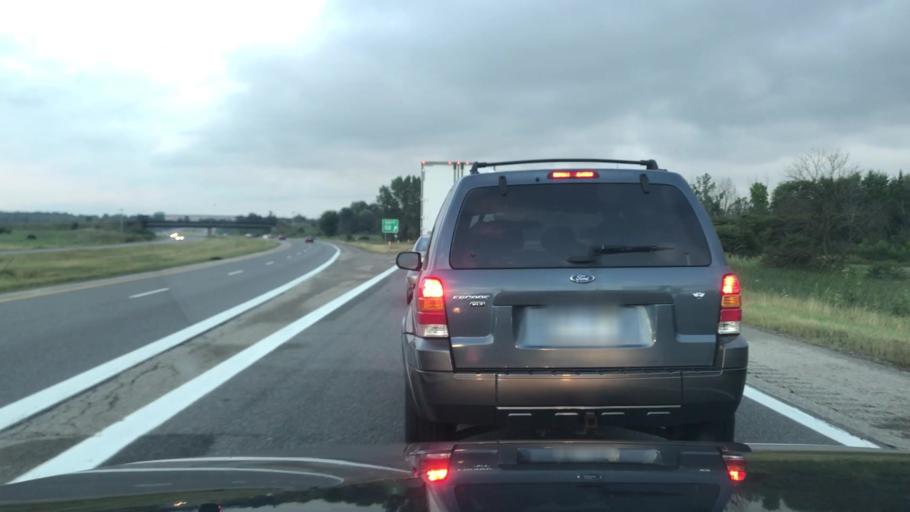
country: US
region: Michigan
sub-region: Ottawa County
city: Zeeland
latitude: 42.7877
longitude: -86.0248
